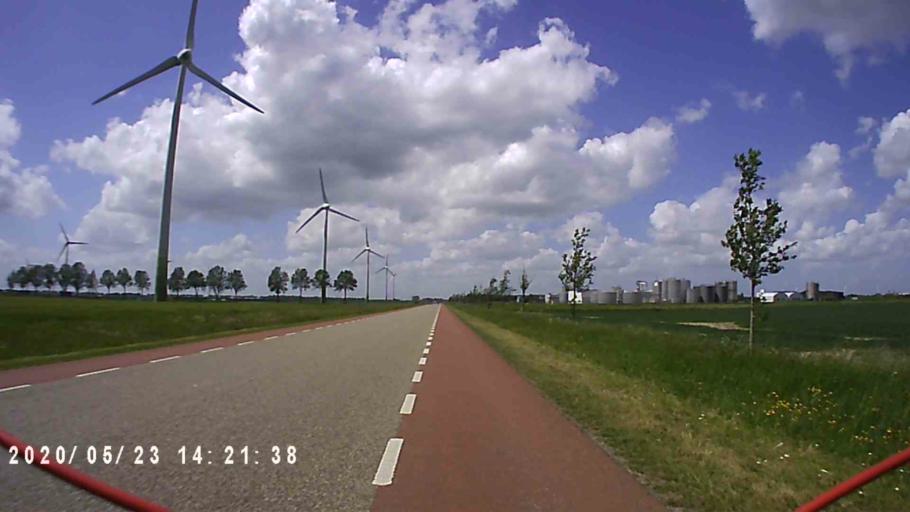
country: NL
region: Groningen
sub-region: Gemeente Delfzijl
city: Delfzijl
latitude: 53.2901
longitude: 6.9809
